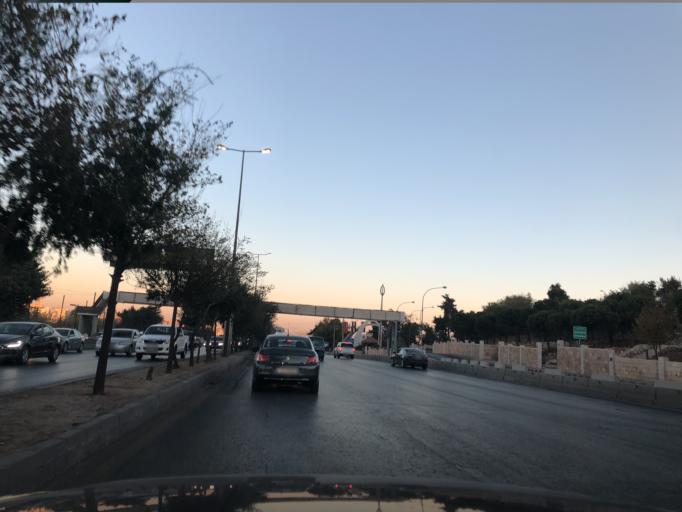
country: JO
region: Amman
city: Wadi as Sir
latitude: 31.9806
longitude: 35.8352
